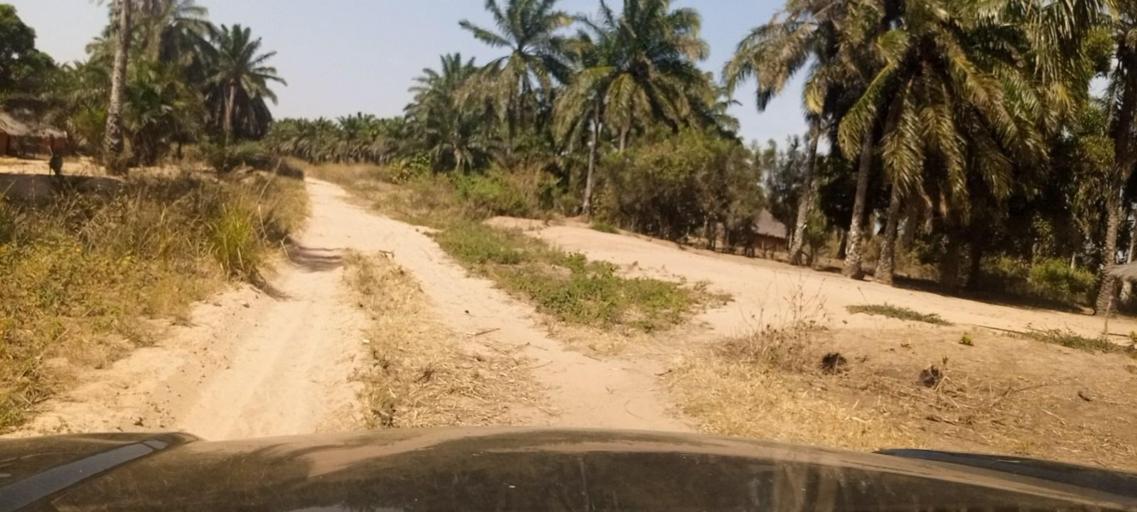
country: CD
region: Kasai-Oriental
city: Kabinda
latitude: -5.8045
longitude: 25.0230
